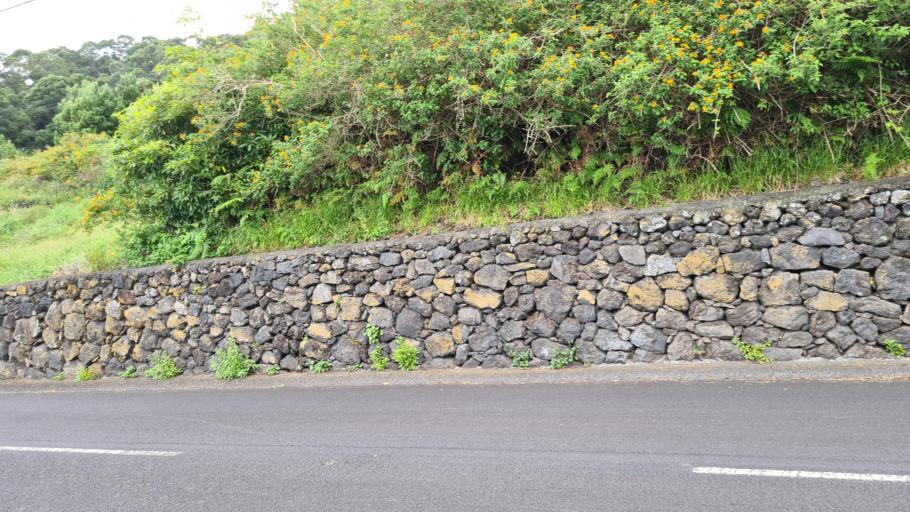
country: PT
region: Azores
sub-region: Sao Roque do Pico
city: Sao Roque do Pico
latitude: 38.6352
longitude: -28.0999
